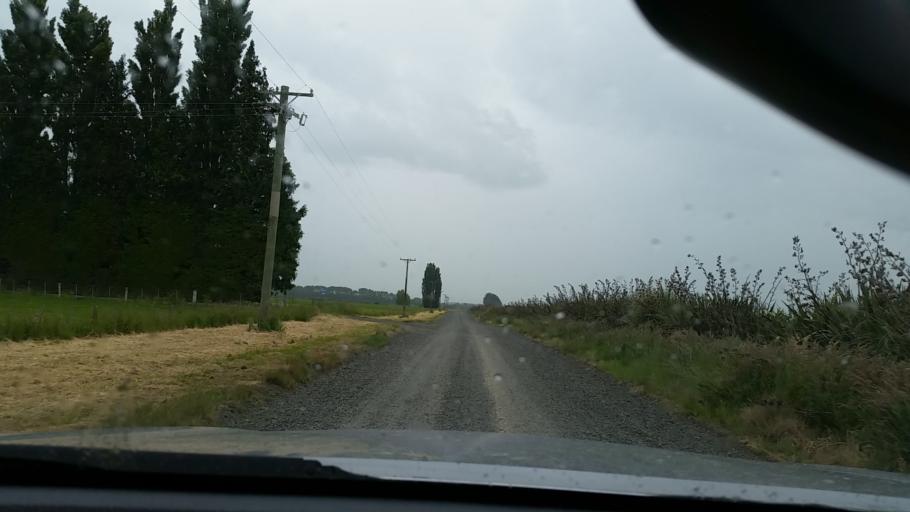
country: NZ
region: Southland
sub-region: Southland District
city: Winton
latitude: -46.0060
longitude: 168.1404
